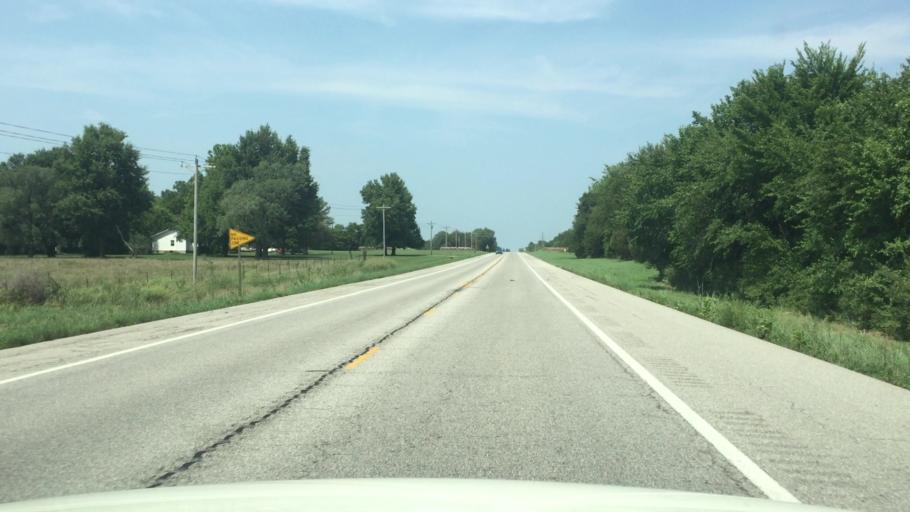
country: US
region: Missouri
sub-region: Jasper County
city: Carl Junction
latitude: 37.2465
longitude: -94.7050
